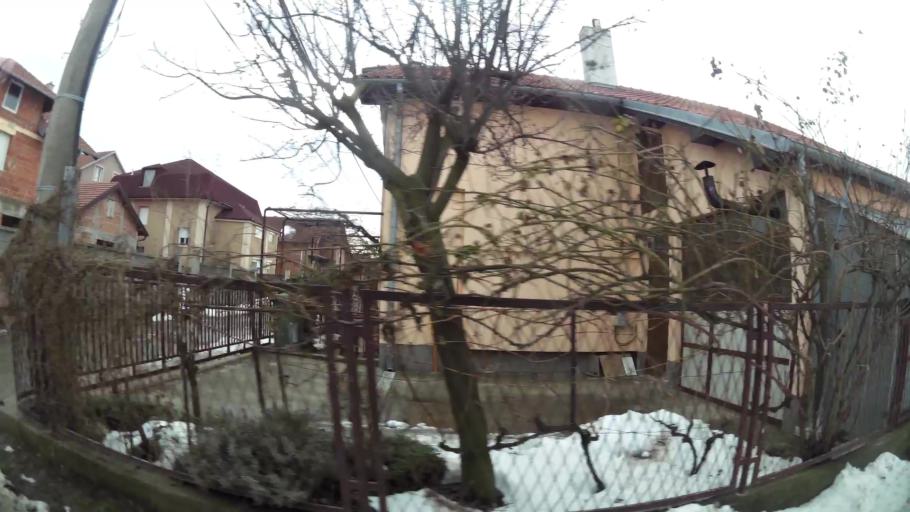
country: RS
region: Central Serbia
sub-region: Belgrade
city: Surcin
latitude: 44.8037
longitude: 20.3296
